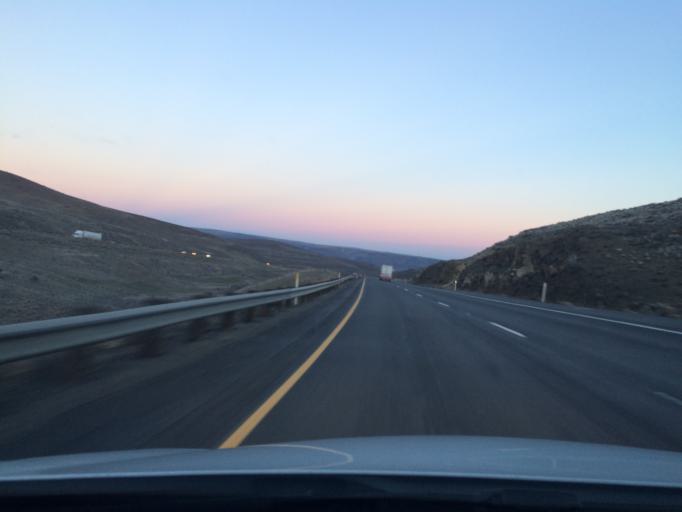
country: US
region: Washington
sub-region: Grant County
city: Mattawa
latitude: 46.9364
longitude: -120.0427
